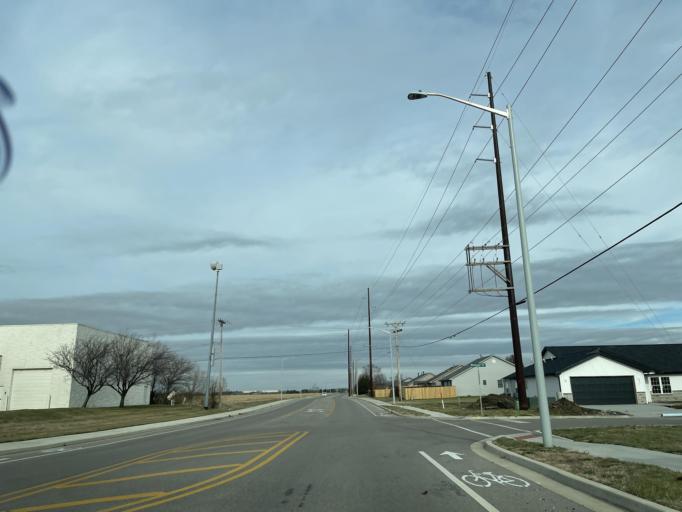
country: US
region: Illinois
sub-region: Sangamon County
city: Jerome
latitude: 39.7593
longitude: -89.7344
